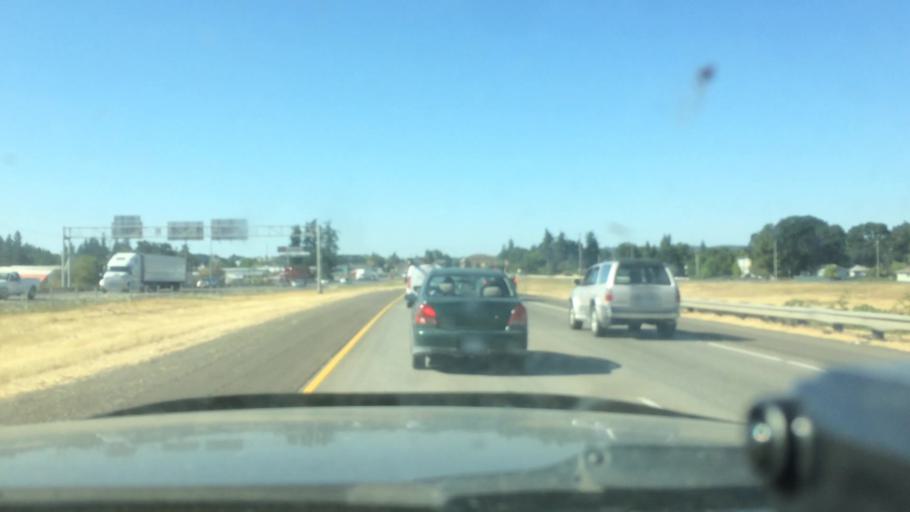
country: US
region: Oregon
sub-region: Linn County
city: Millersburg
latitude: 44.6455
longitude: -123.0622
